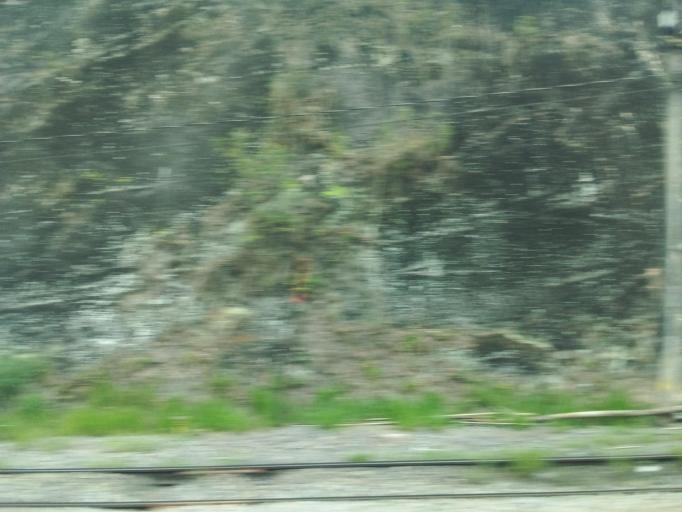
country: BR
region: Minas Gerais
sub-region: Joao Monlevade
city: Joao Monlevade
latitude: -19.8467
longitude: -43.1238
